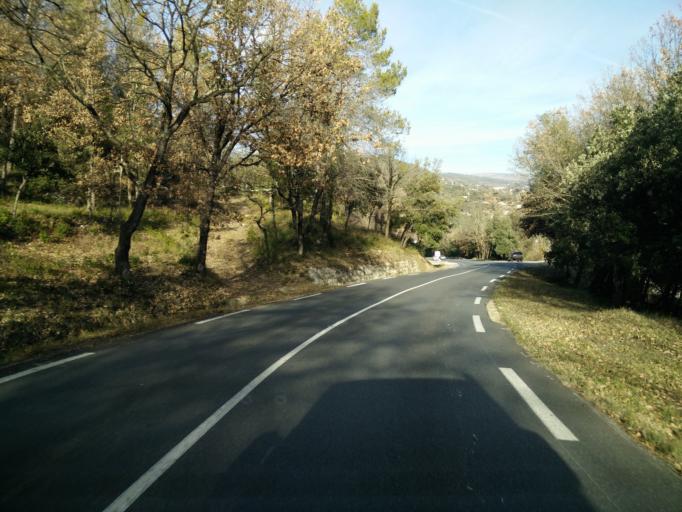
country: FR
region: Provence-Alpes-Cote d'Azur
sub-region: Departement des Alpes-Maritimes
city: Le Tignet
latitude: 43.6175
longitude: 6.8225
